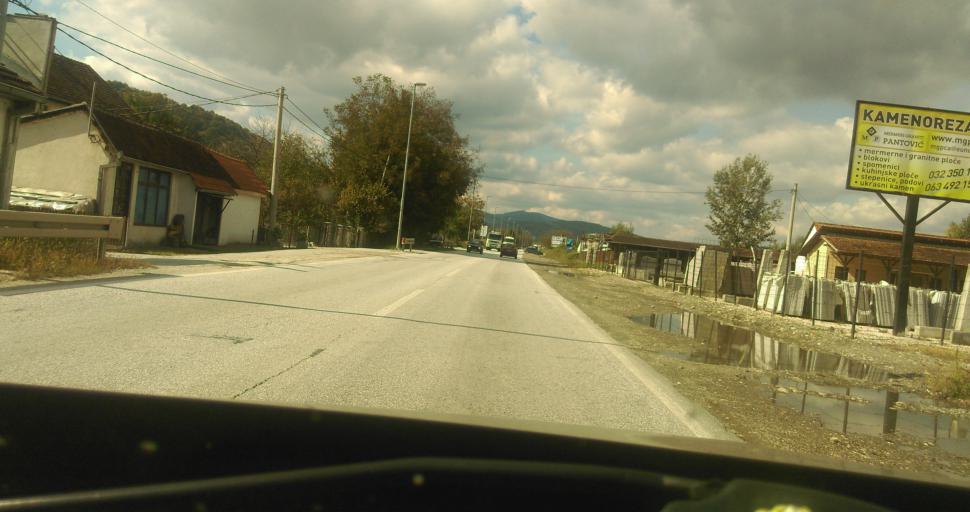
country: RS
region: Central Serbia
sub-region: Moravicki Okrug
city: Cacak
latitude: 43.8928
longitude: 20.3054
